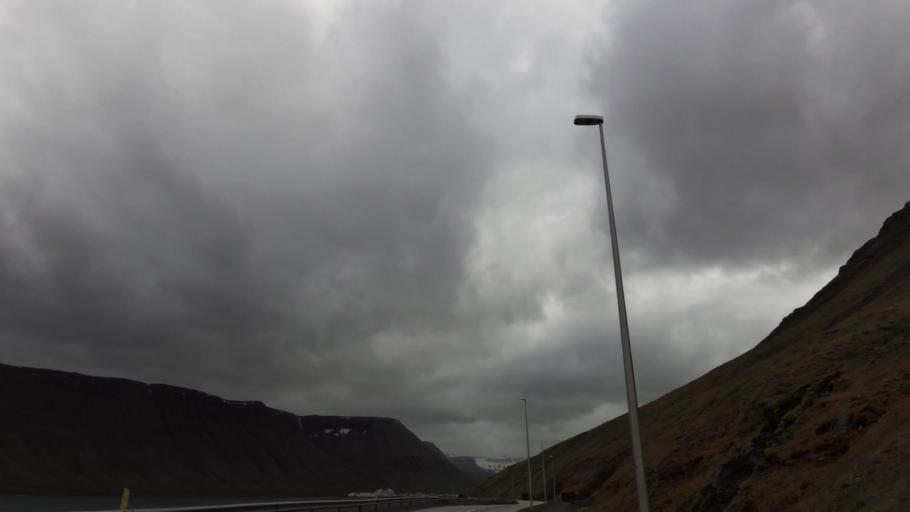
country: IS
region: Westfjords
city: Isafjoerdur
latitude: 66.0962
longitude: -23.1117
